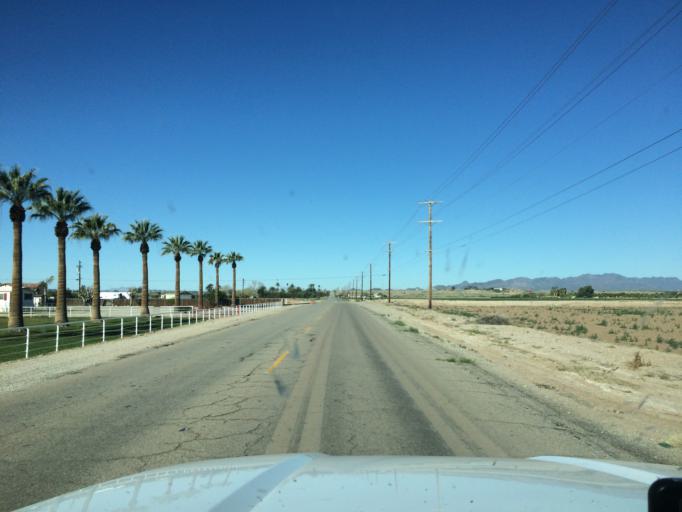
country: US
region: California
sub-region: Riverside County
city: Blythe
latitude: 33.6101
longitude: -114.6473
